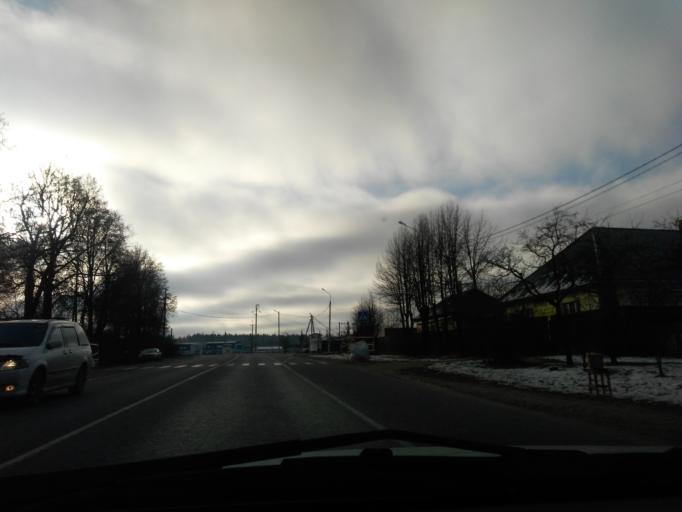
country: RU
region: Moskovskaya
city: Selyatino
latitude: 55.2786
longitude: 37.1158
